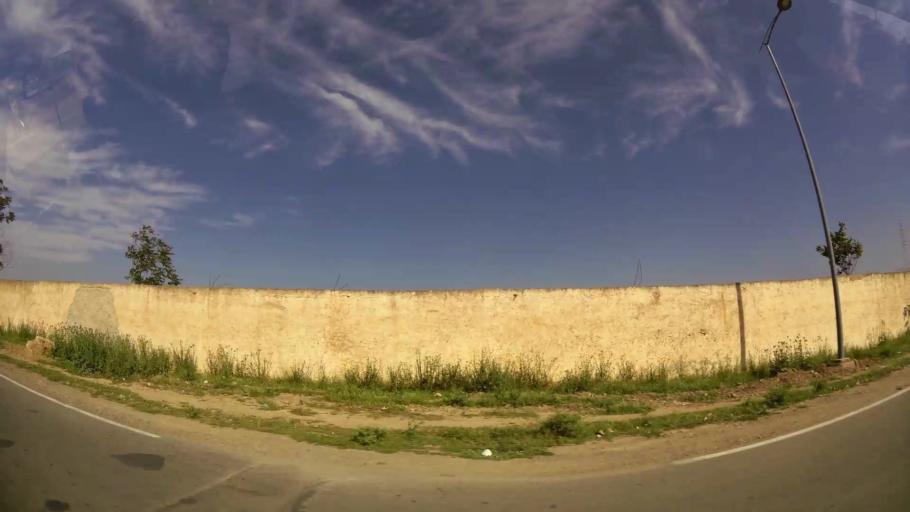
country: MA
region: Oriental
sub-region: Oujda-Angad
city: Oujda
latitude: 34.7205
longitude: -1.8808
